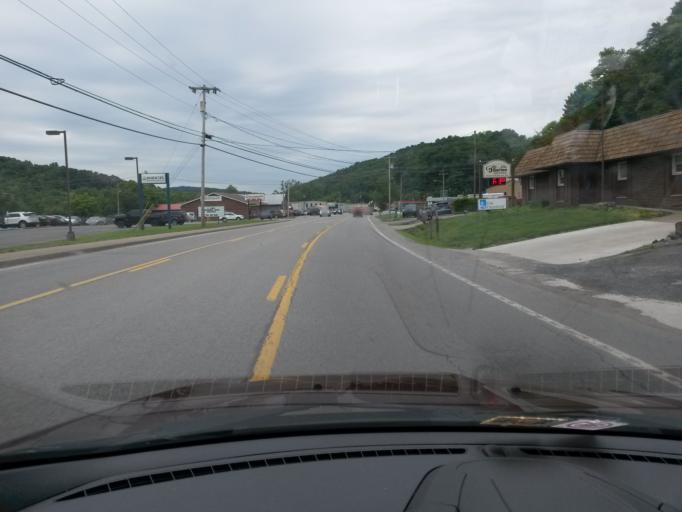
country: US
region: West Virginia
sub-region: Lewis County
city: Weston
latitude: 39.0366
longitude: -80.4534
